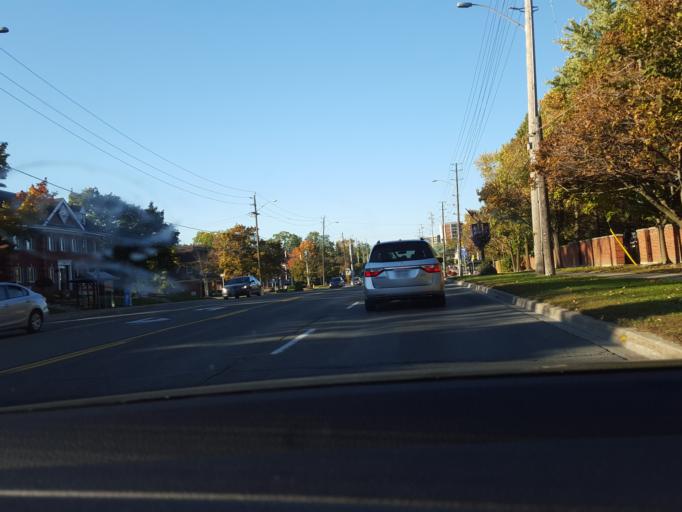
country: CA
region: Ontario
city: North York
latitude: 43.8131
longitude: -79.4237
